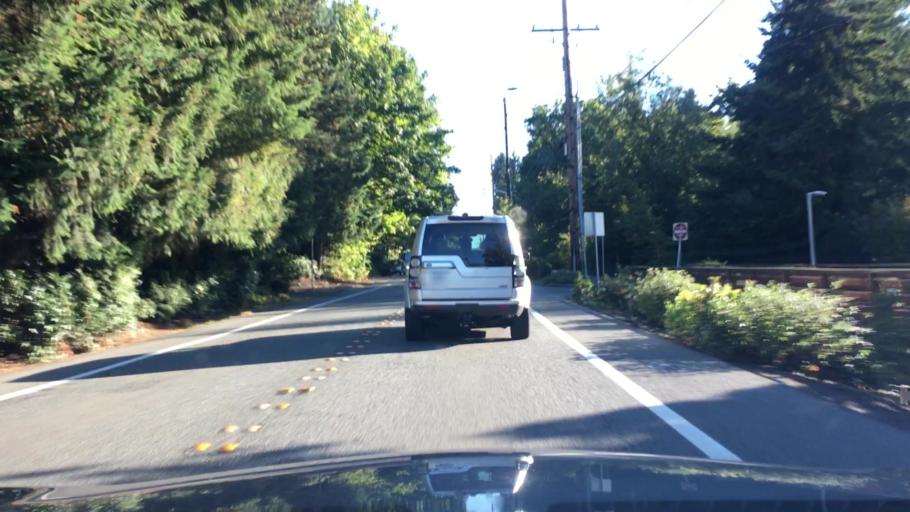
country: US
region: Washington
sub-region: King County
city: Bellevue
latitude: 47.5966
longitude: -122.1829
